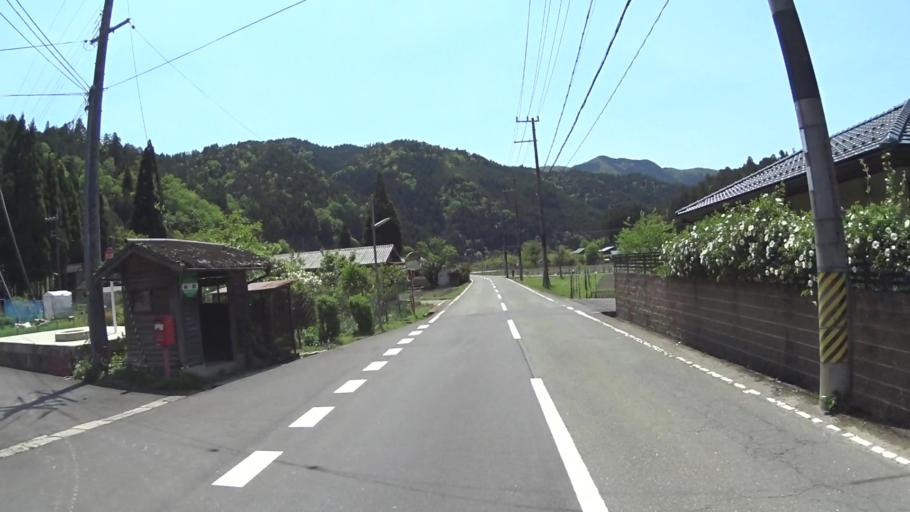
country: JP
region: Kyoto
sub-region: Kyoto-shi
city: Kamigyo-ku
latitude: 35.2012
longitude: 135.6824
